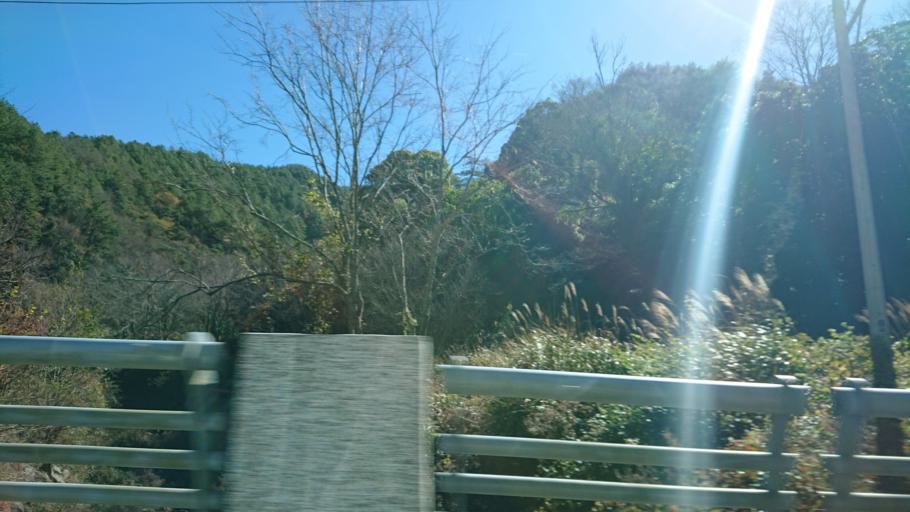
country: TW
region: Taiwan
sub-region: Hualien
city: Hualian
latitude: 24.3663
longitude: 121.3374
